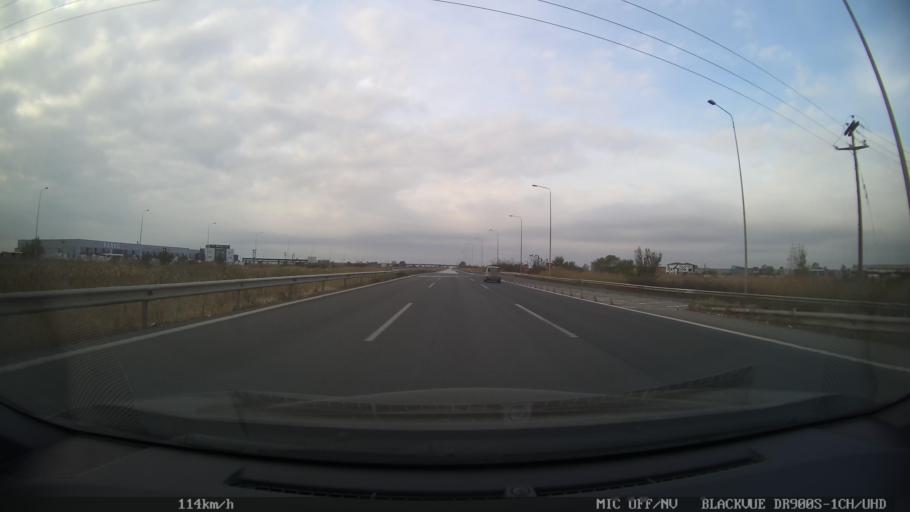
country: GR
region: Central Macedonia
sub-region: Nomos Thessalonikis
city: Sindos
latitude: 40.6493
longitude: 22.8104
